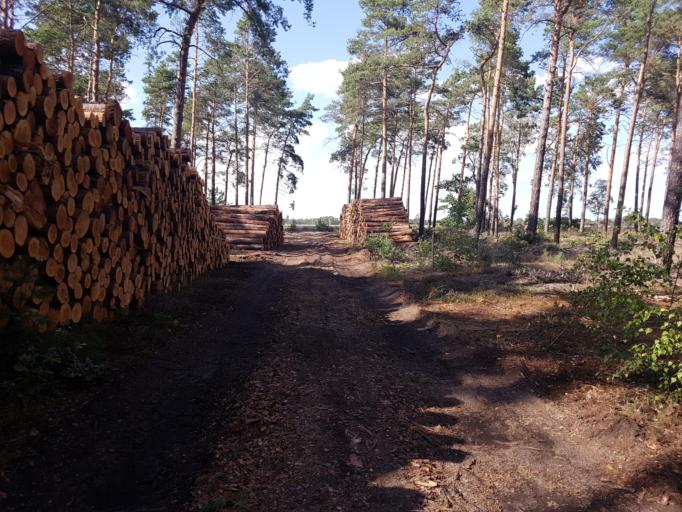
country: DE
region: Brandenburg
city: Finsterwalde
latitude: 51.6321
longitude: 13.6730
